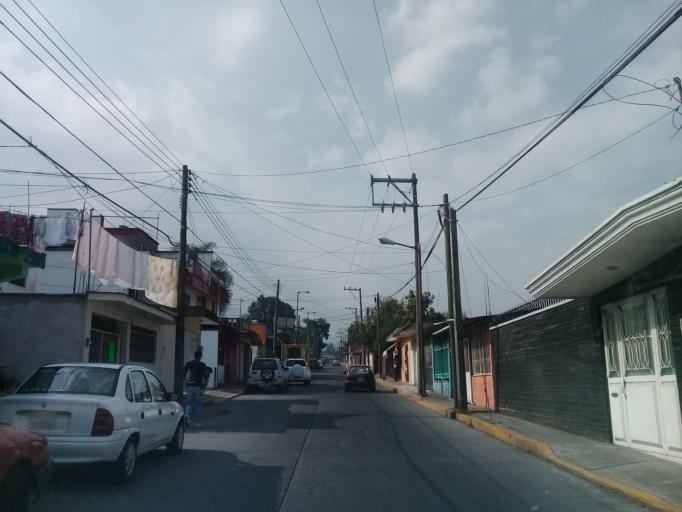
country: MX
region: Veracruz
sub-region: Ixhuatlancillo
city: Union y Progreso
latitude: 18.8664
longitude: -97.1078
